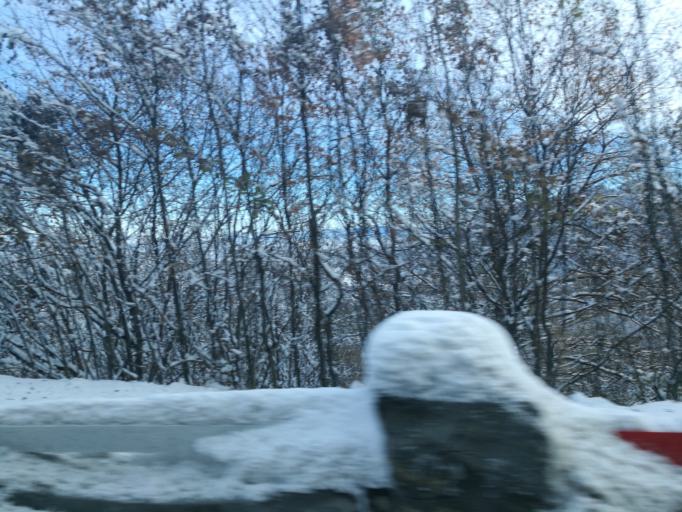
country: RO
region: Brasov
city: Brasov
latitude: 45.6372
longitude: 25.5645
